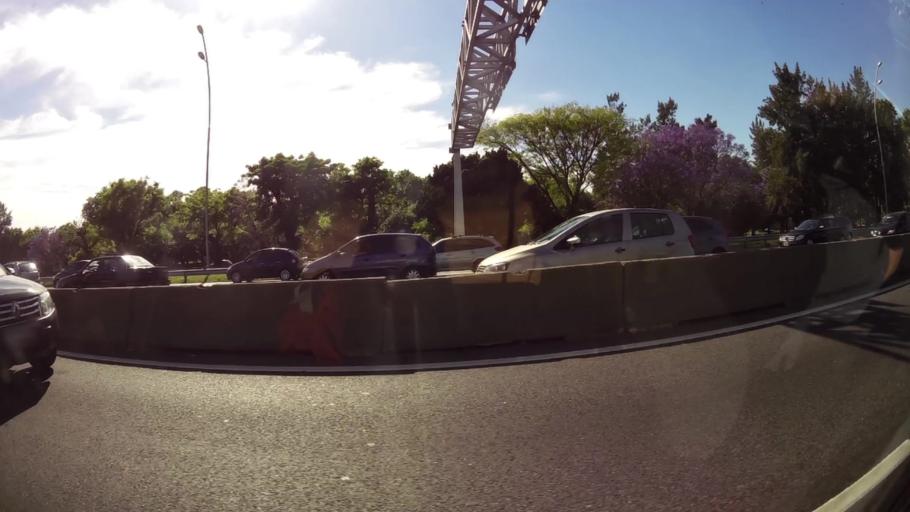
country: AR
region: Buenos Aires
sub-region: Partido de General San Martin
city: General San Martin
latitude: -34.5627
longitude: -58.5062
